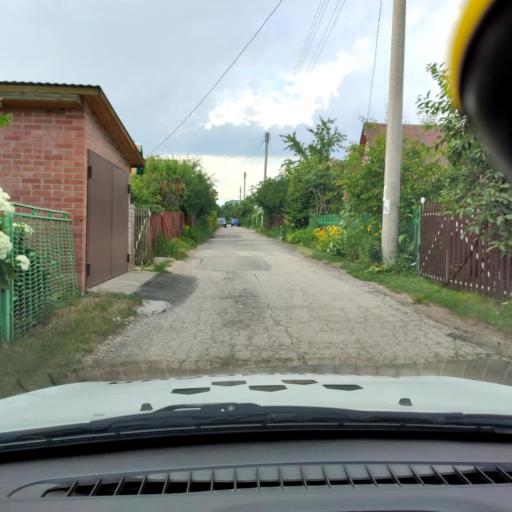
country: RU
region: Samara
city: Podstepki
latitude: 53.5062
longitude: 49.1440
